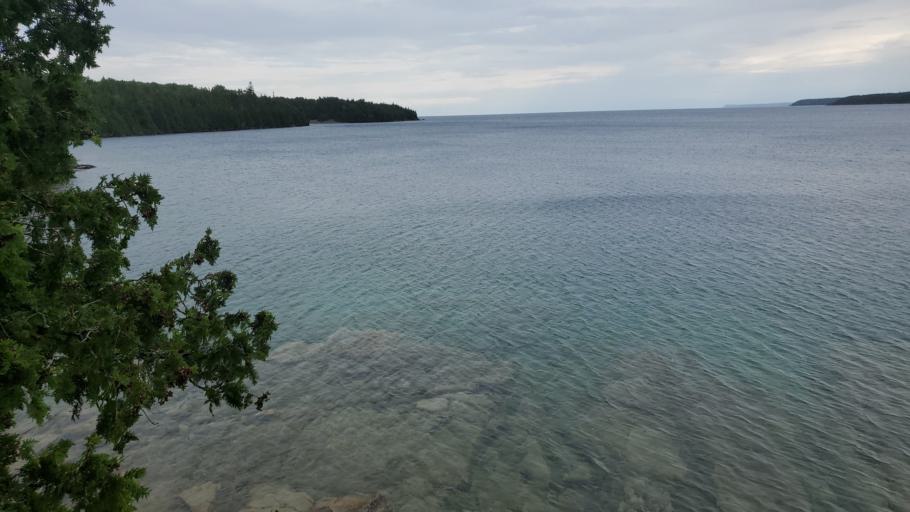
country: CA
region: Ontario
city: Tobermory
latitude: 45.2581
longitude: -81.6468
